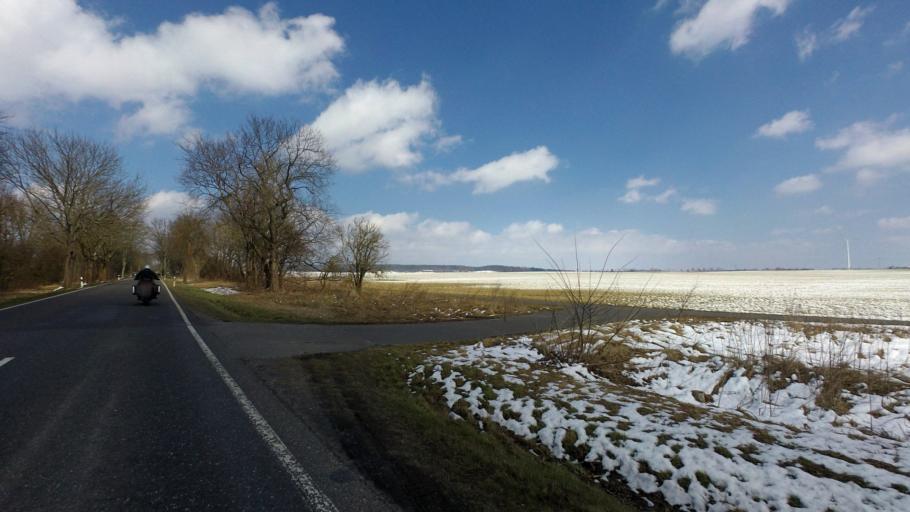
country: DE
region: Brandenburg
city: Britz
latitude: 52.8739
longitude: 13.7458
